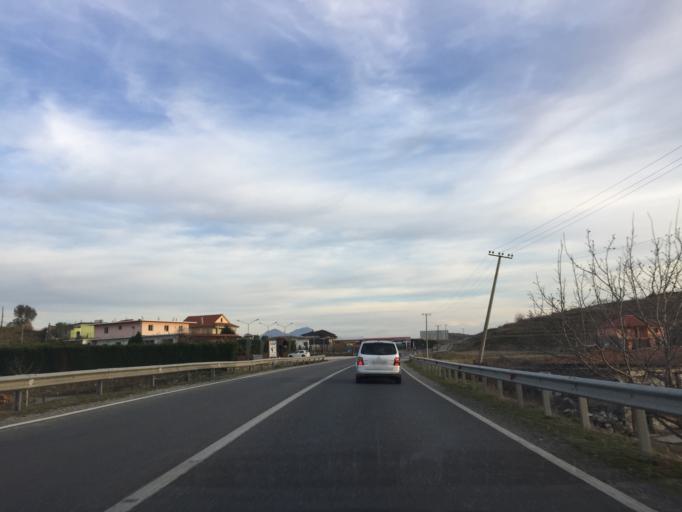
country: AL
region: Shkoder
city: Vukatane
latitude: 41.9661
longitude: 19.5499
